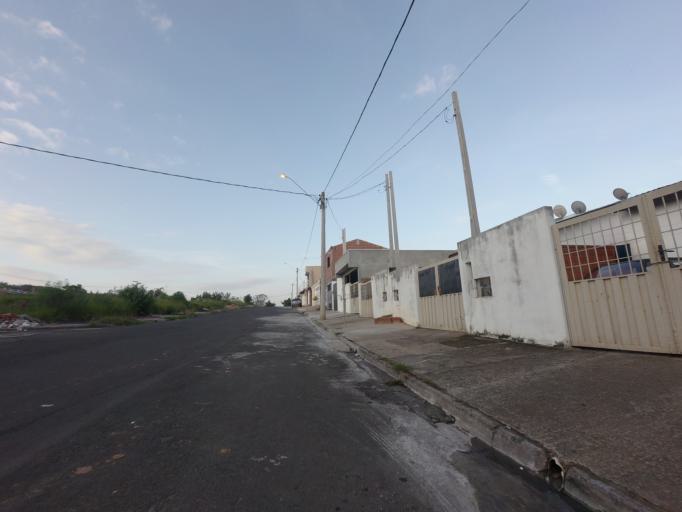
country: BR
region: Sao Paulo
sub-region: Piracicaba
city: Piracicaba
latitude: -22.7628
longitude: -47.6088
